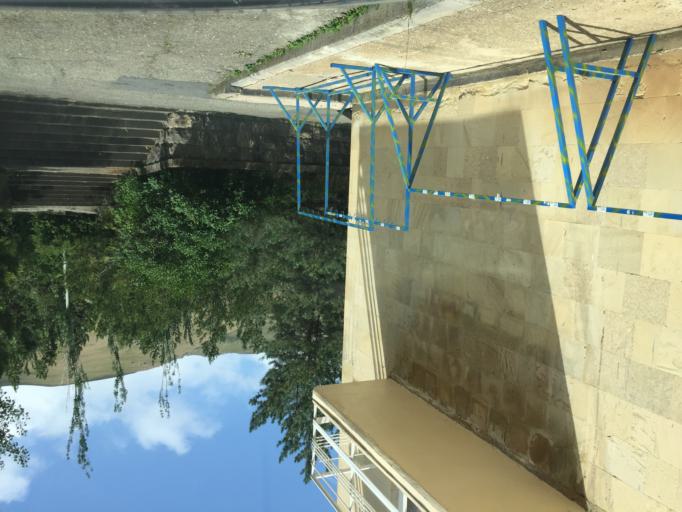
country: AM
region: Geghark'unik'i Marz
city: Tsovagyugh
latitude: 40.6210
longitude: 45.0169
